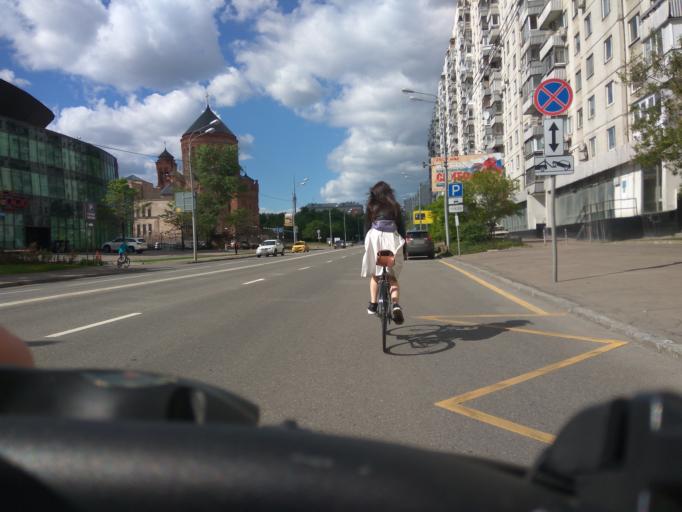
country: RU
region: Moscow
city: Mar'ina Roshcha
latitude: 55.7864
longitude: 37.6226
